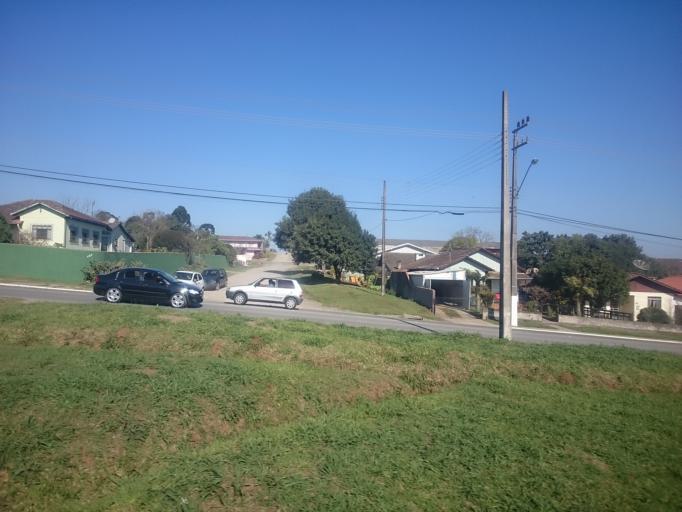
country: BR
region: Parana
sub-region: Rio Negro
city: Rio Negro
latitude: -26.0845
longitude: -49.7769
